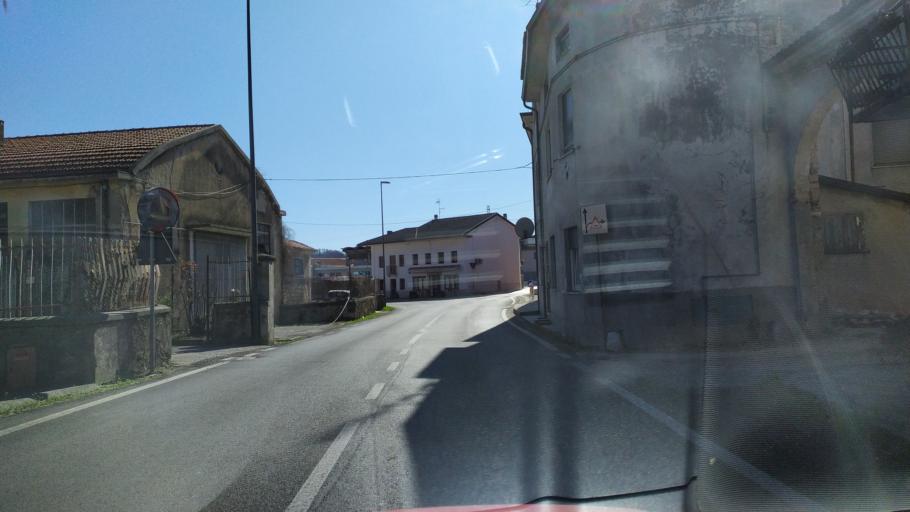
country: IT
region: Veneto
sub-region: Provincia di Vicenza
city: Chiuppano
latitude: 45.7671
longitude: 11.4586
